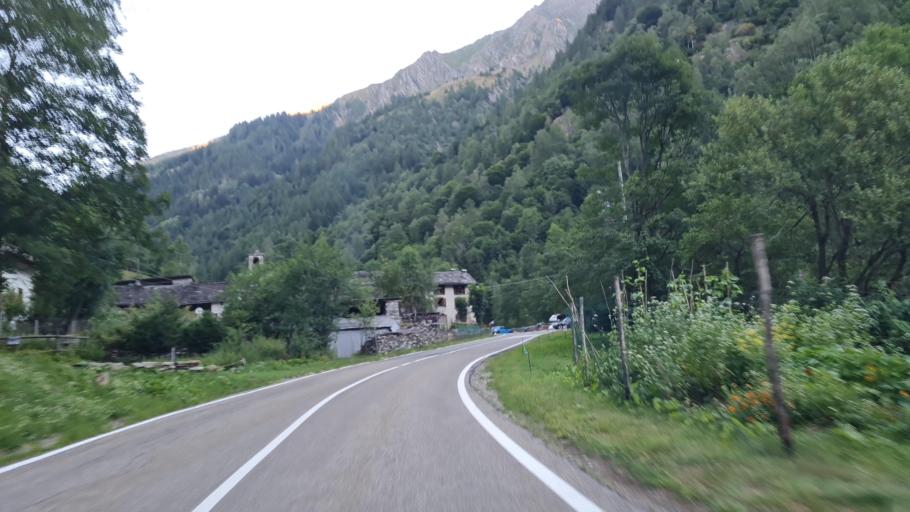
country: IT
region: Piedmont
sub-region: Provincia di Vercelli
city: Rima
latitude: 45.8717
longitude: 8.0193
